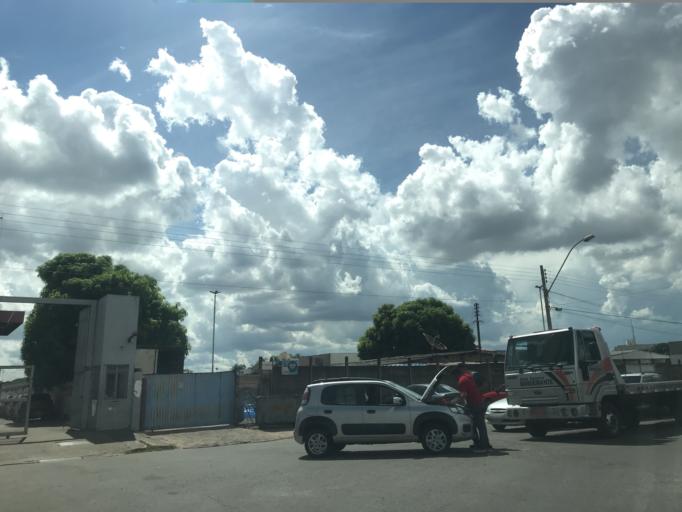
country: BR
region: Federal District
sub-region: Brasilia
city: Brasilia
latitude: -15.8387
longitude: -48.0446
